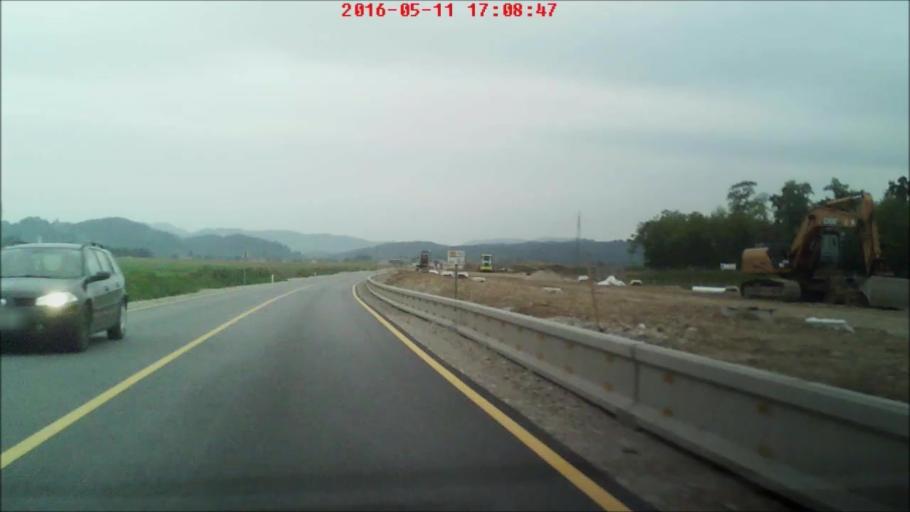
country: SI
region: Hajdina
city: Spodnja Hajdina
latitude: 46.3824
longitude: 15.8660
